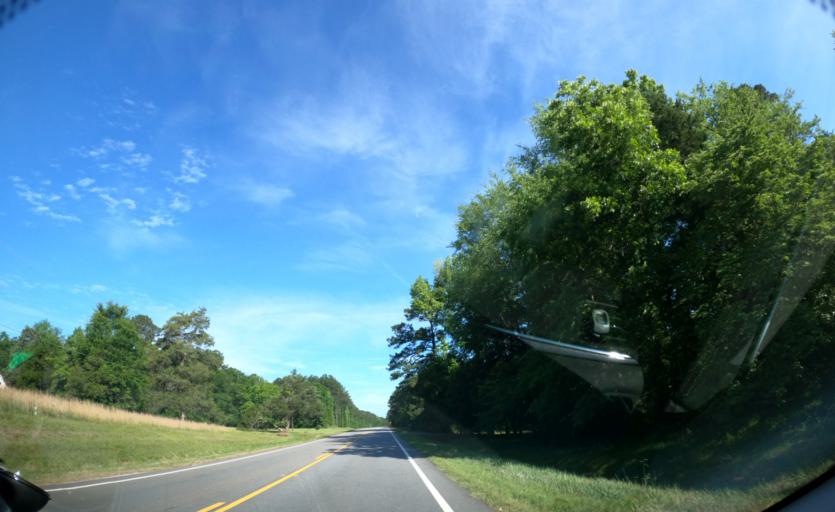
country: US
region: Georgia
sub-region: Columbia County
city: Appling
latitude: 33.6326
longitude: -82.2956
